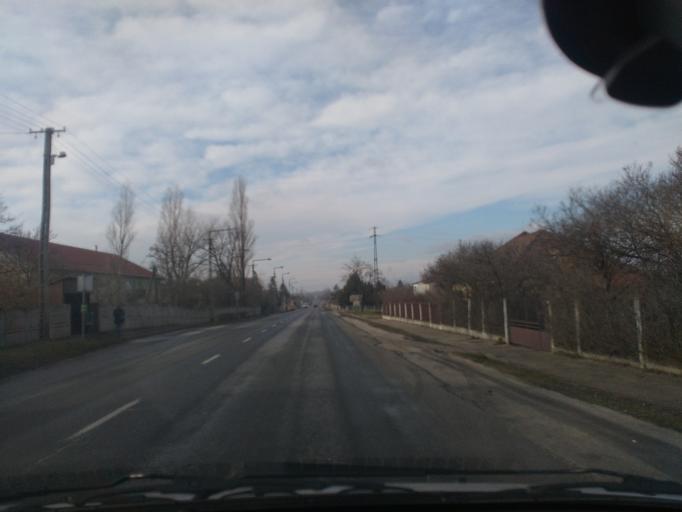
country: HU
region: Komarom-Esztergom
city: Tokod
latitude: 47.7315
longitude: 18.6937
